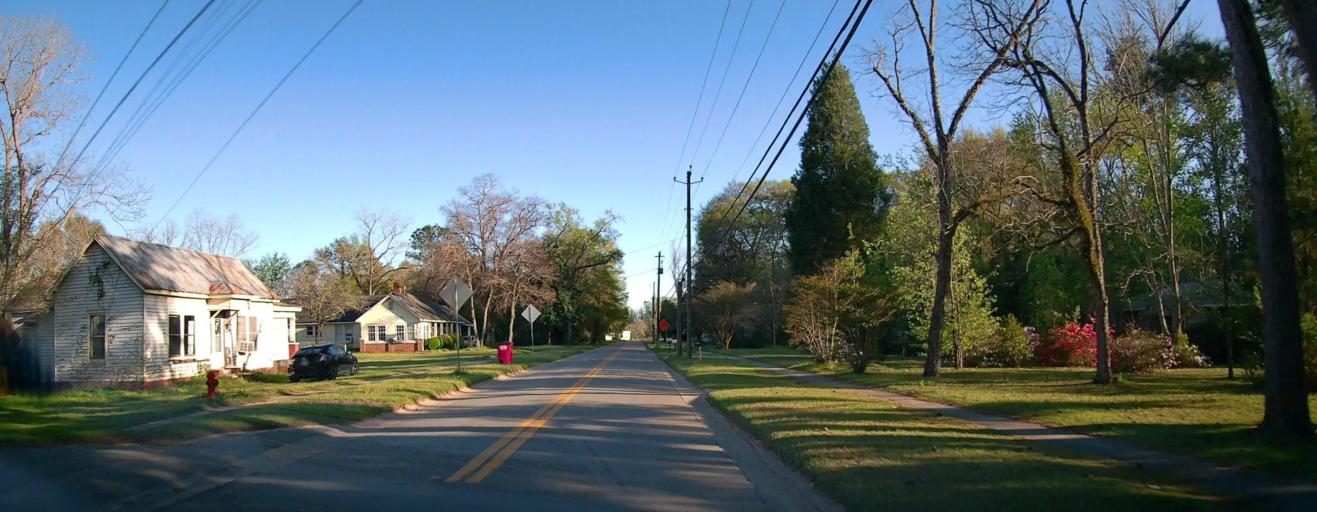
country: US
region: Georgia
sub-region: Wilkinson County
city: Irwinton
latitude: 32.8254
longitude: -83.0797
